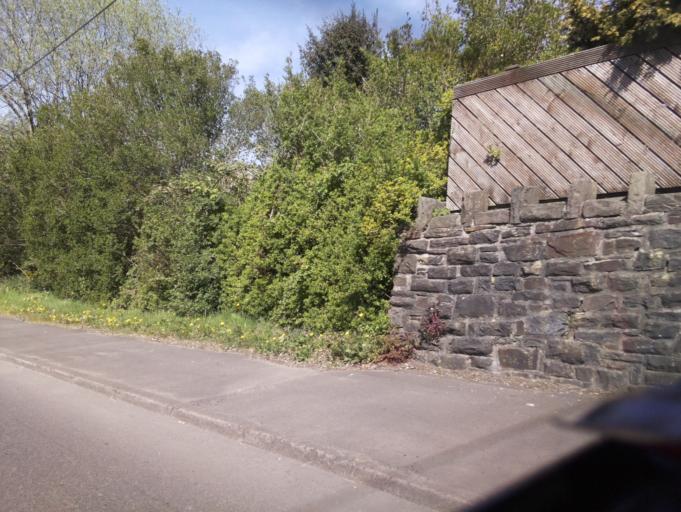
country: GB
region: Wales
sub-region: Rhondda Cynon Taf
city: Cwmbach
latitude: 51.7006
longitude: -3.4119
